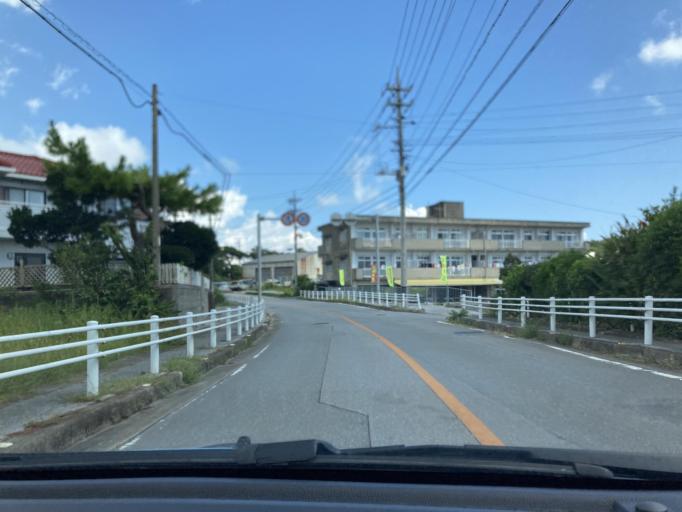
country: JP
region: Okinawa
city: Tomigusuku
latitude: 26.1504
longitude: 127.7916
